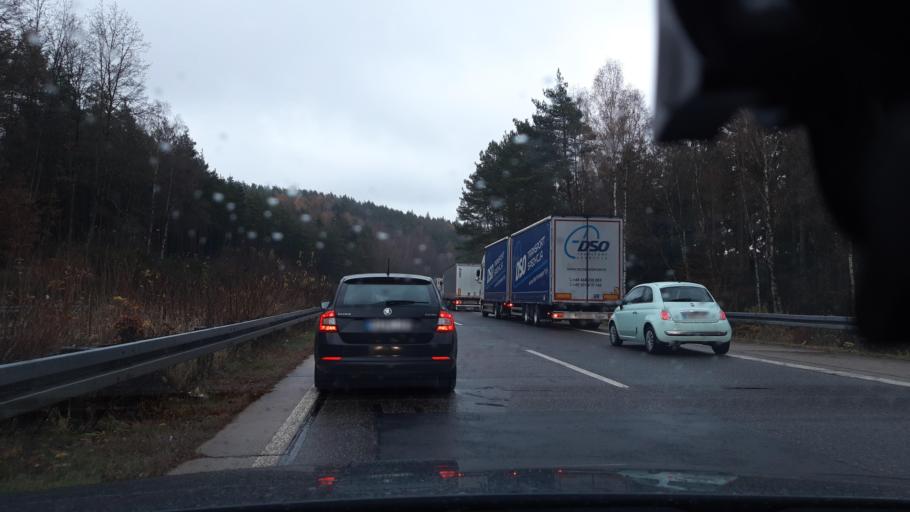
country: DE
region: Hesse
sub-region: Regierungsbezirk Kassel
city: Kirchheim
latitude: 50.8059
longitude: 9.5232
